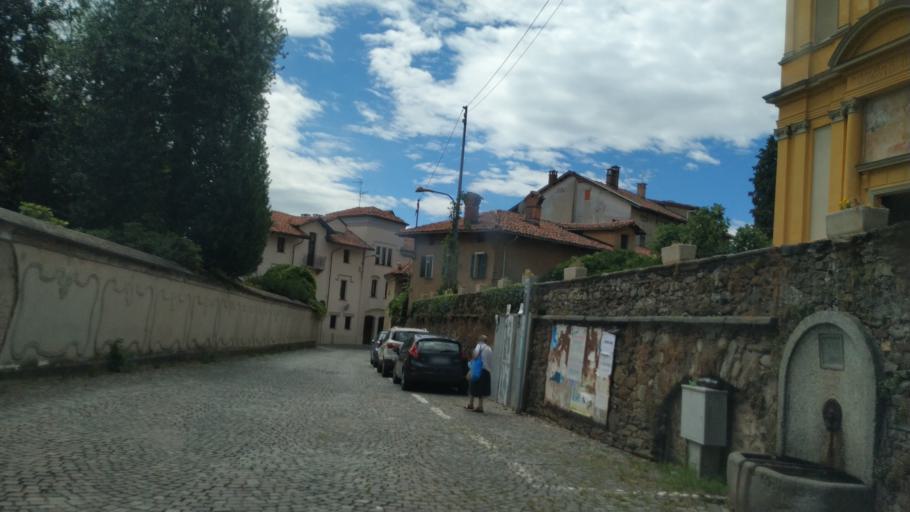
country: IT
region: Piedmont
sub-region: Provincia di Biella
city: Pollone
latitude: 45.5828
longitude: 8.0003
